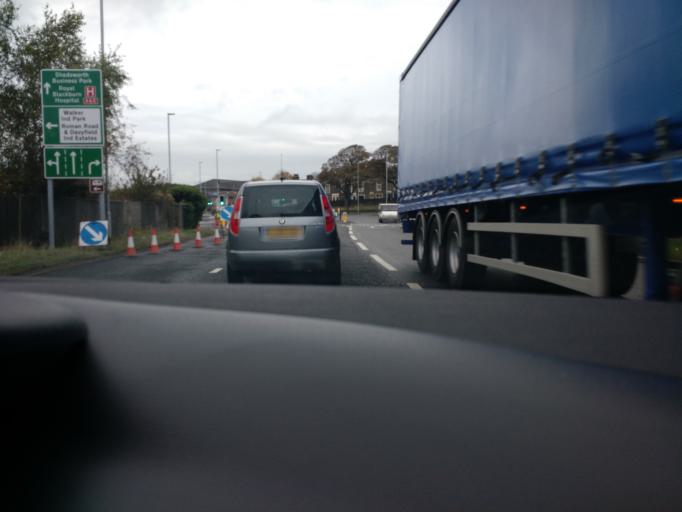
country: GB
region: England
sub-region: Blackburn with Darwen
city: Darwen
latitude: 53.7271
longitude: -2.4483
